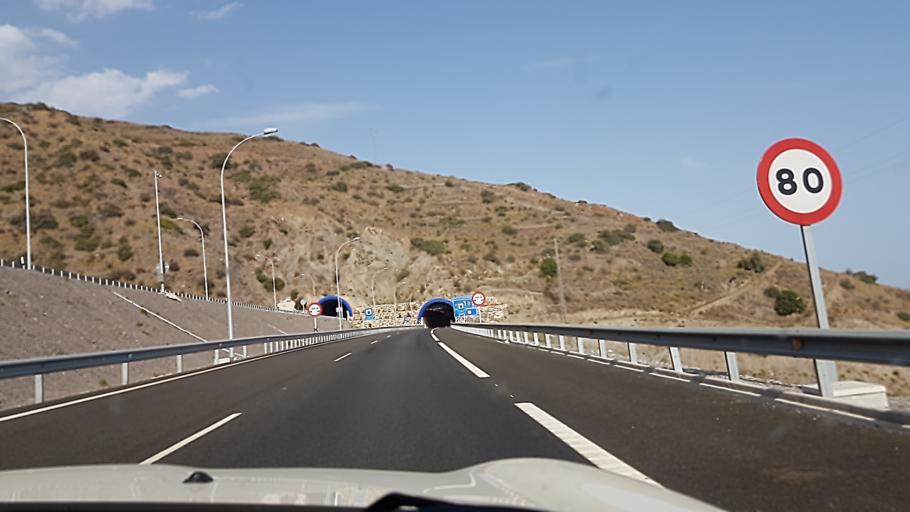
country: ES
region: Andalusia
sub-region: Provincia de Granada
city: Sorvilan
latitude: 36.7565
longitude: -3.2575
